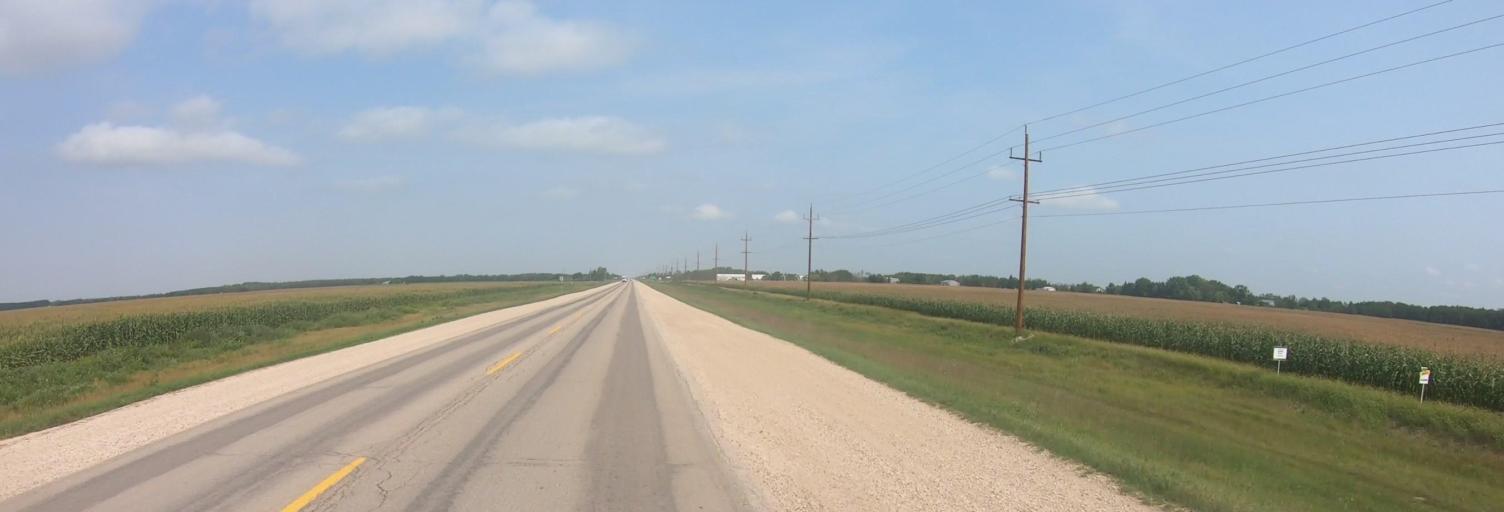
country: CA
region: Manitoba
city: Steinbach
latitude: 49.4680
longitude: -96.6911
